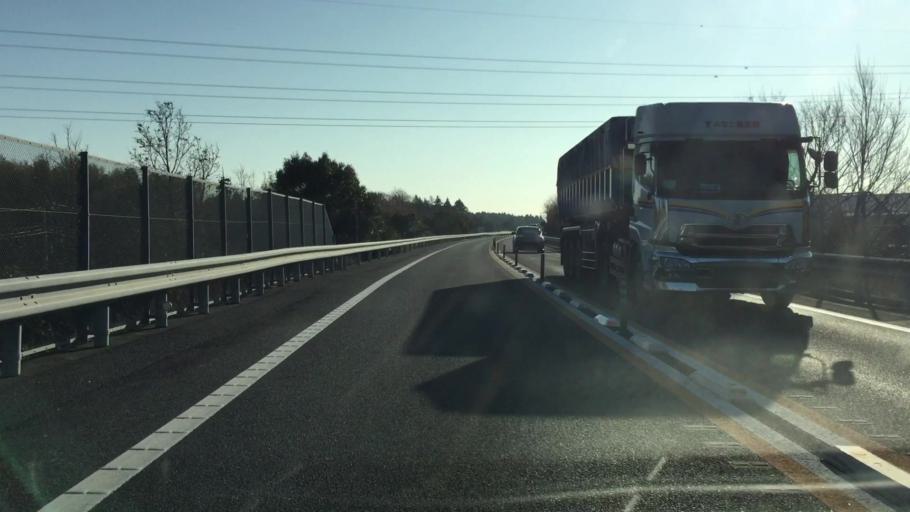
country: JP
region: Ibaraki
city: Ami
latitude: 35.9940
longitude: 140.2133
